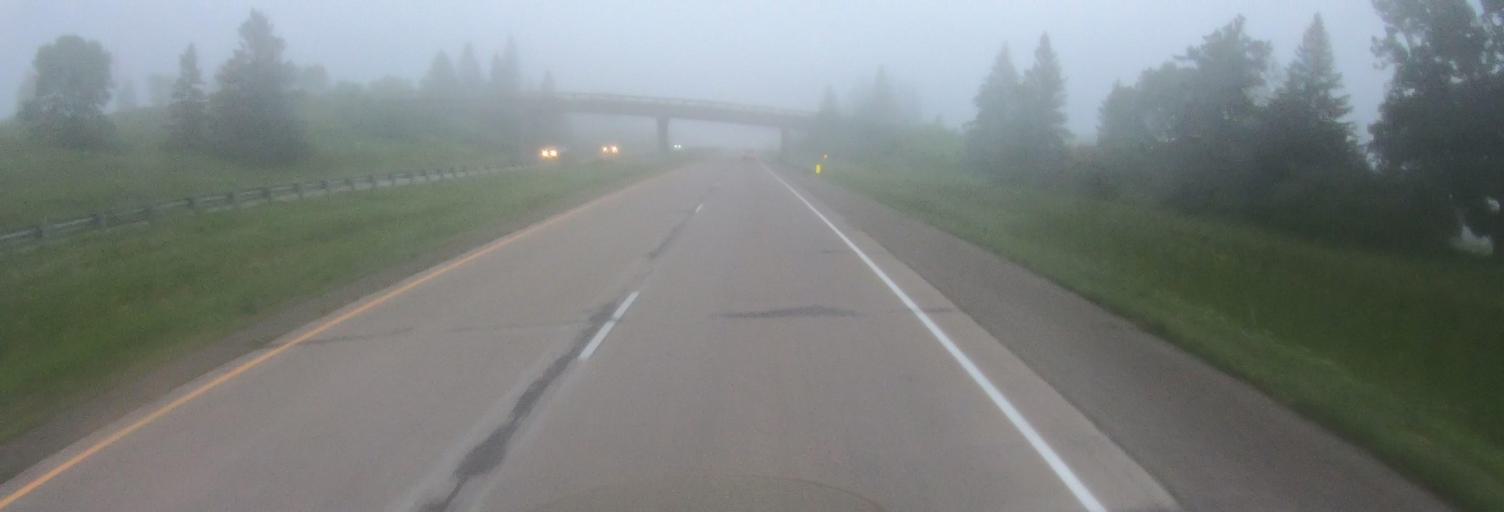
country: US
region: Minnesota
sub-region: Carlton County
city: Moose Lake
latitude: 46.5045
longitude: -92.6754
